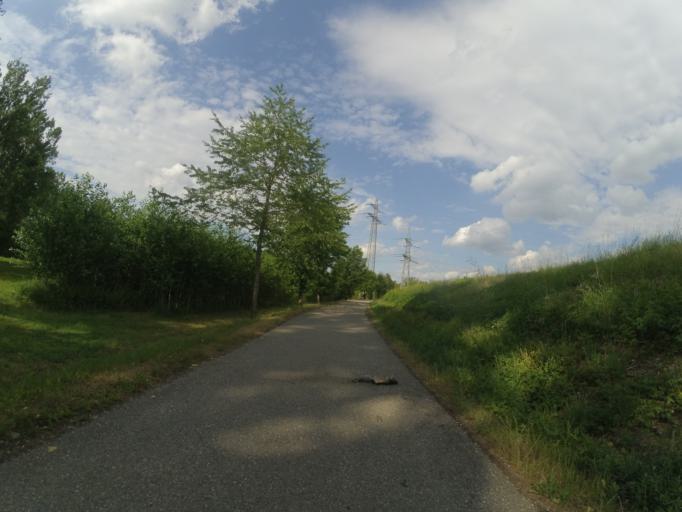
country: DE
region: Baden-Wuerttemberg
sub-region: Tuebingen Region
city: Erbach
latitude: 48.3150
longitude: 9.8754
